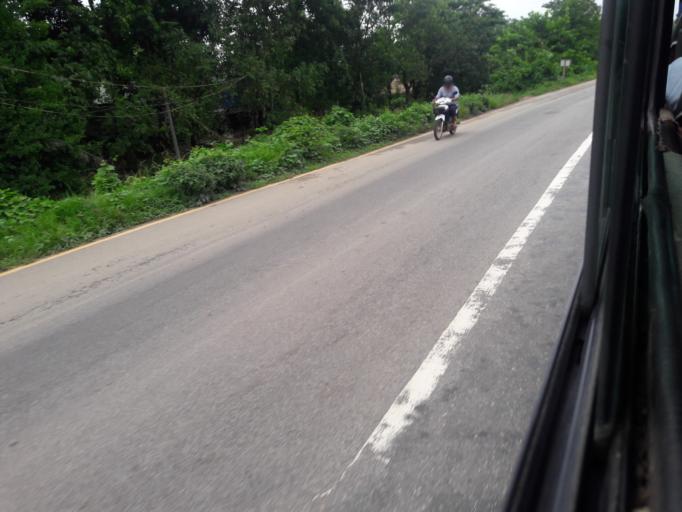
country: MM
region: Bago
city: Nyaunglebin
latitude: 17.8384
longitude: 96.6814
